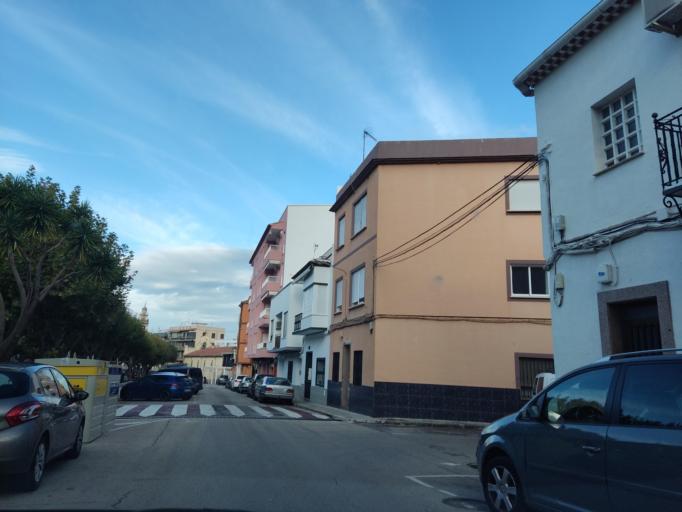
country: ES
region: Valencia
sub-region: Provincia de Alicante
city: Pego
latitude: 38.8389
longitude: -0.1206
